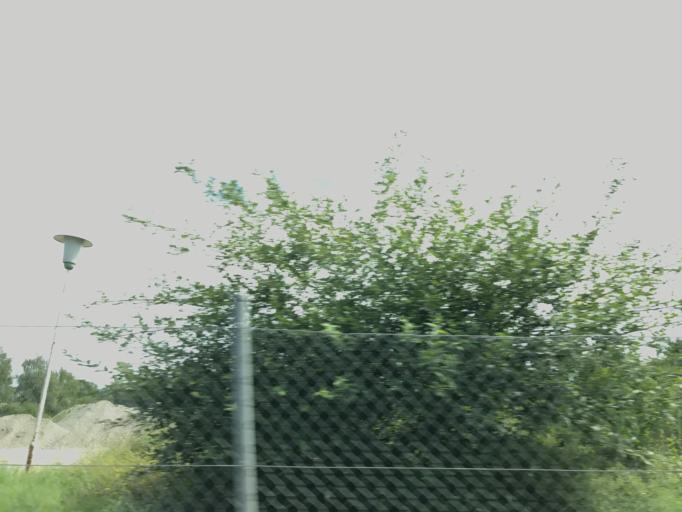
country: DE
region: Baden-Wuerttemberg
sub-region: Tuebingen Region
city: Saulgau
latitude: 48.0239
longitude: 9.4897
